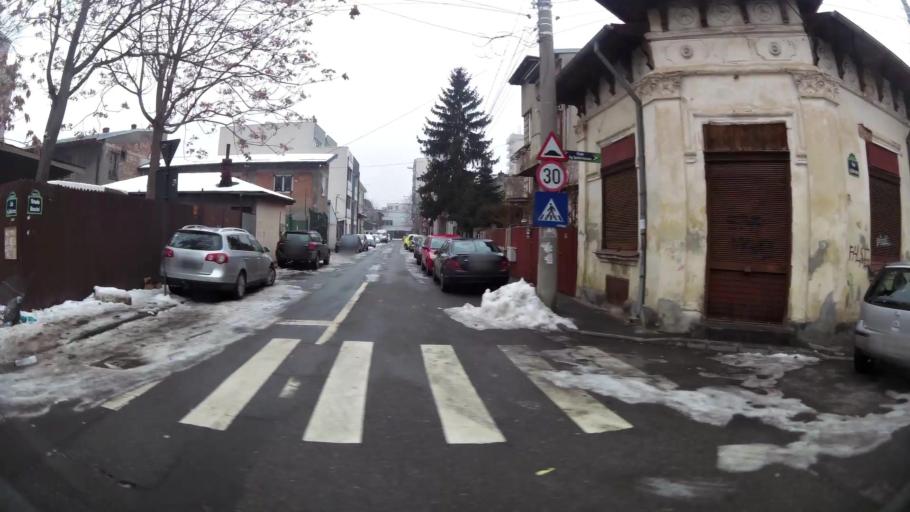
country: RO
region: Bucuresti
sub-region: Municipiul Bucuresti
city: Bucharest
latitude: 44.4500
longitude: 26.1136
